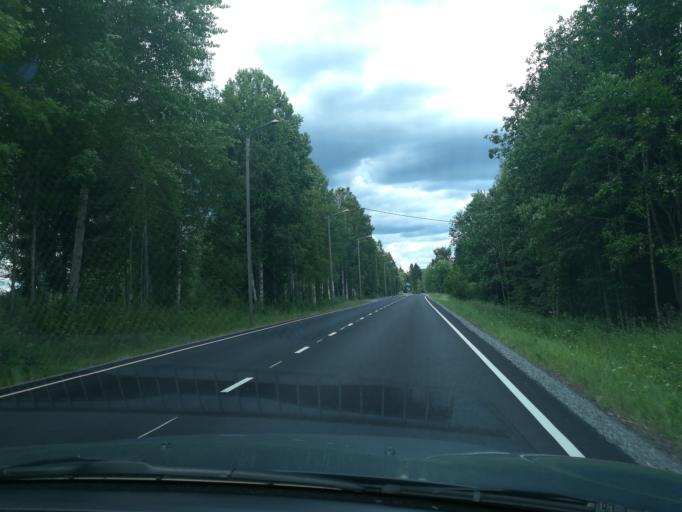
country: FI
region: Southern Savonia
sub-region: Mikkeli
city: Mikkeli
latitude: 61.6455
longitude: 27.0810
